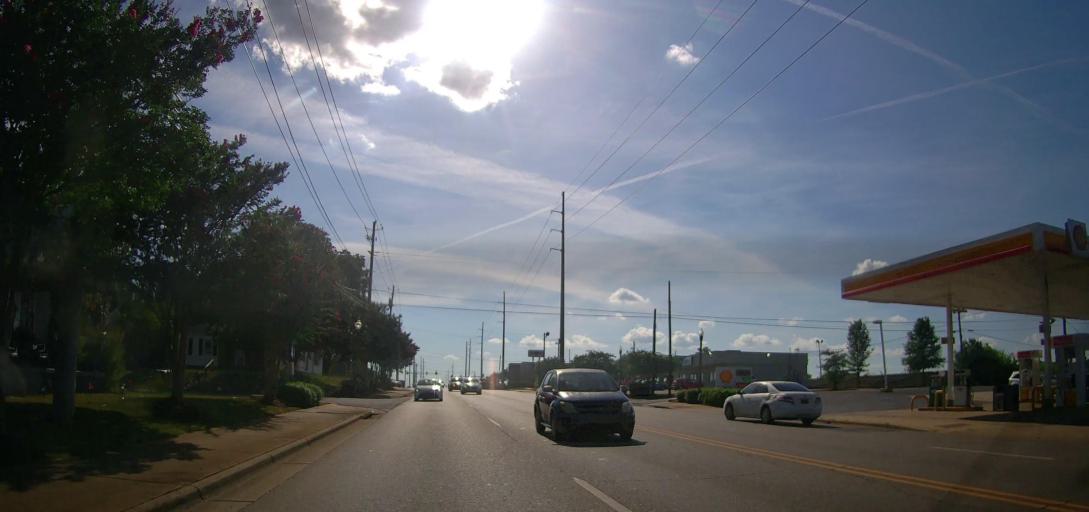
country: US
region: Alabama
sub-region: Tuscaloosa County
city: Holt
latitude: 33.2064
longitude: -87.4996
